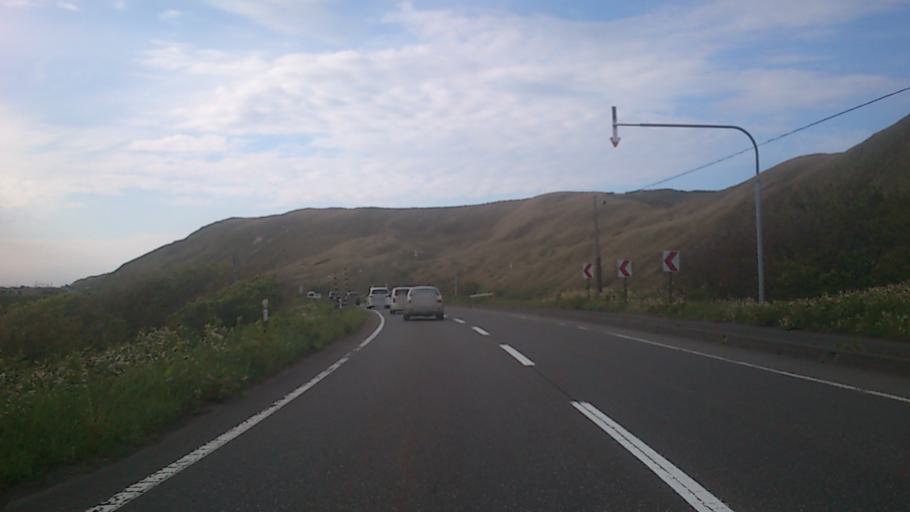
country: JP
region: Hokkaido
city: Wakkanai
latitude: 45.3672
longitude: 141.6617
